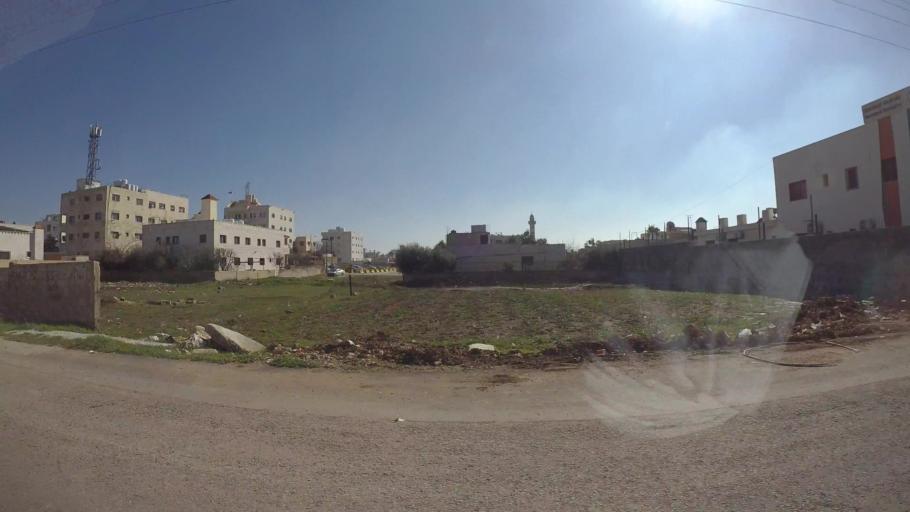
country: JO
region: Amman
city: Al Bunayyat ash Shamaliyah
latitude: 31.9048
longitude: 35.8936
